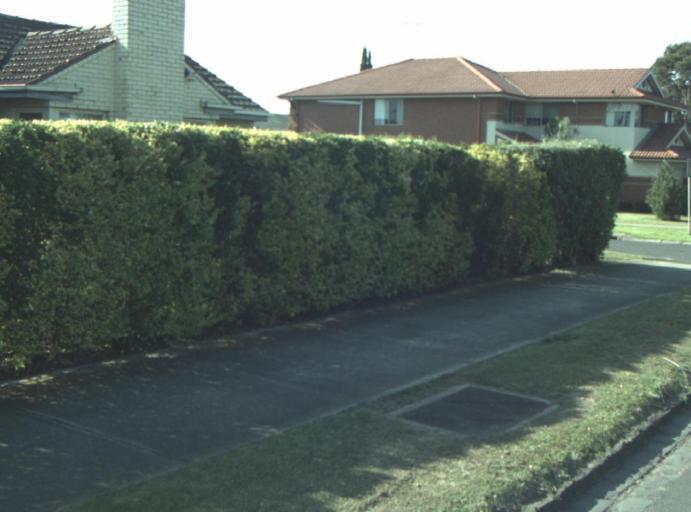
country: AU
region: Victoria
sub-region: Greater Geelong
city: Geelong West
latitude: -38.1202
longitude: 144.3536
